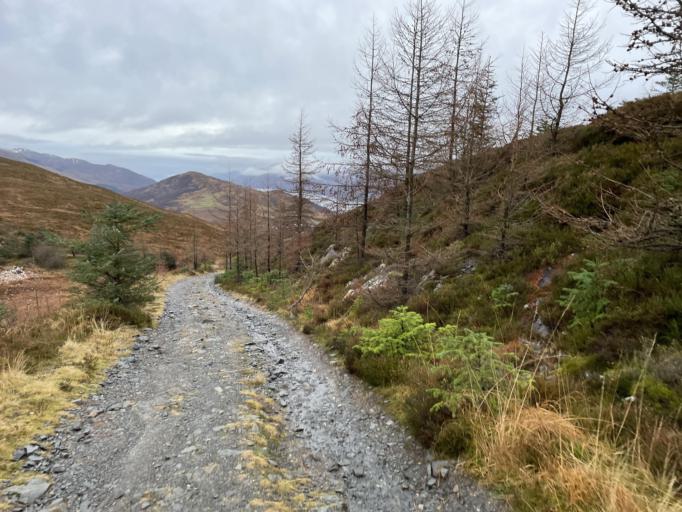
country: GB
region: Scotland
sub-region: Highland
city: Fort William
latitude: 56.8138
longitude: -5.0938
